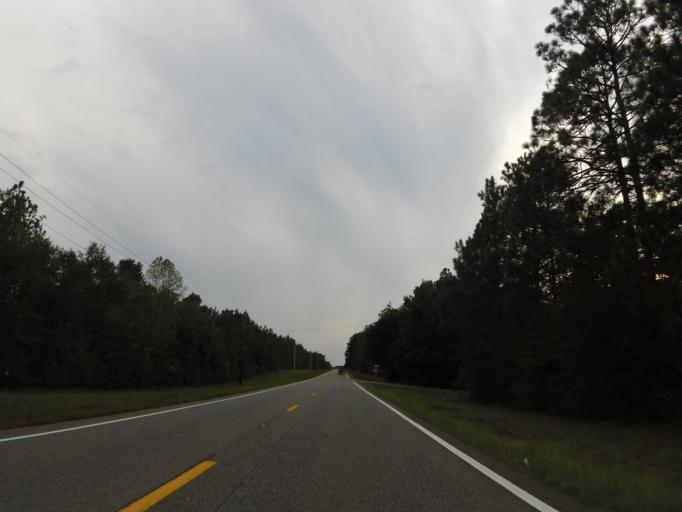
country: US
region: Alabama
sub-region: Baldwin County
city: Bay Minette
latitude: 30.9041
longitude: -87.7302
